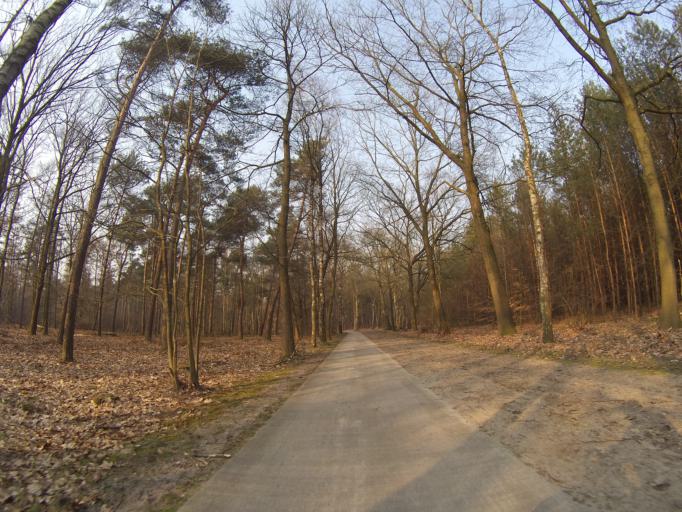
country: NL
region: Utrecht
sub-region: Gemeente Soest
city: Soest
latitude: 52.1457
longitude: 5.3241
